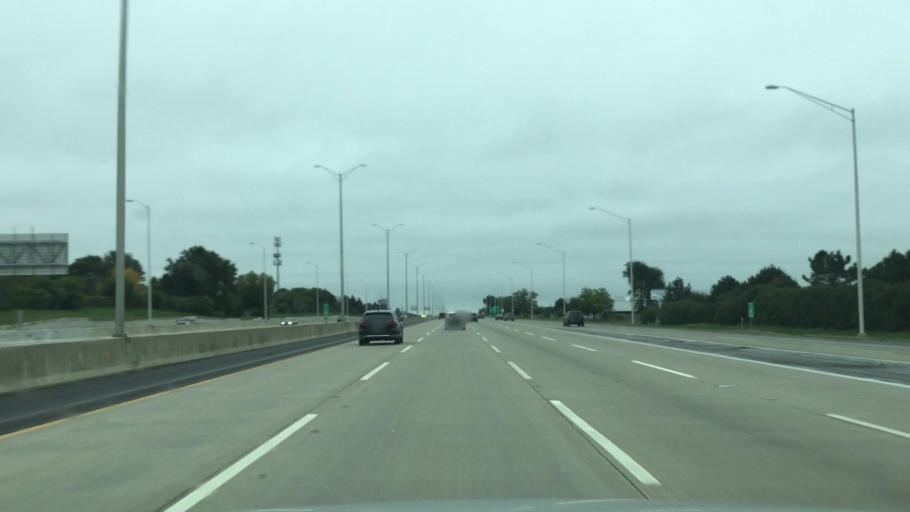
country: US
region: Illinois
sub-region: Lake County
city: Grandwood Park
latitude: 42.3775
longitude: -87.9459
